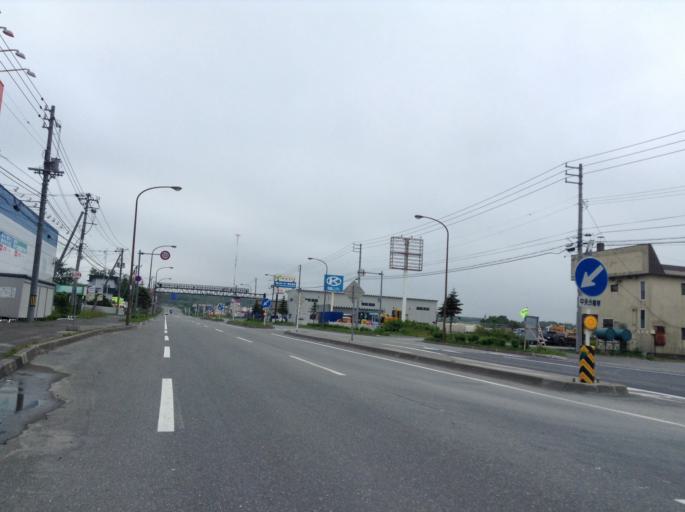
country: JP
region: Hokkaido
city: Wakkanai
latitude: 45.3825
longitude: 141.7085
